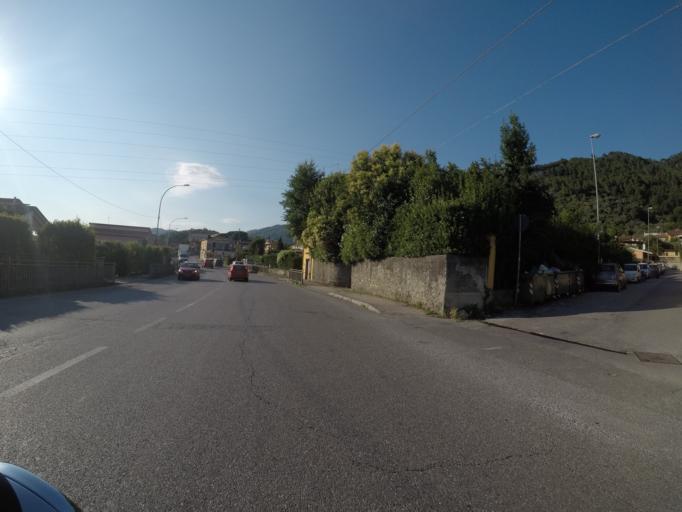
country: IT
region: Tuscany
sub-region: Provincia di Massa-Carrara
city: San Vito-Cerreto
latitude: 44.0243
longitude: 10.1462
